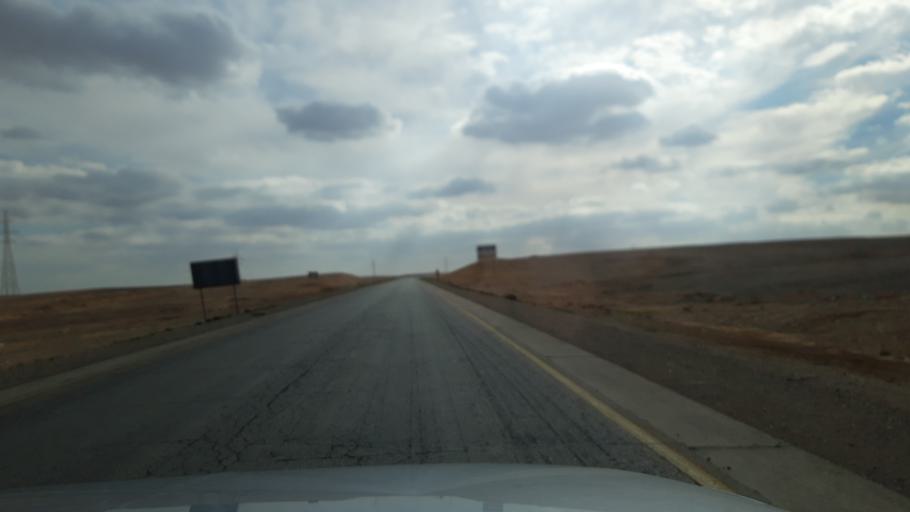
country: JO
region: Amman
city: Al Azraq ash Shamali
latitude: 31.7468
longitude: 36.5382
